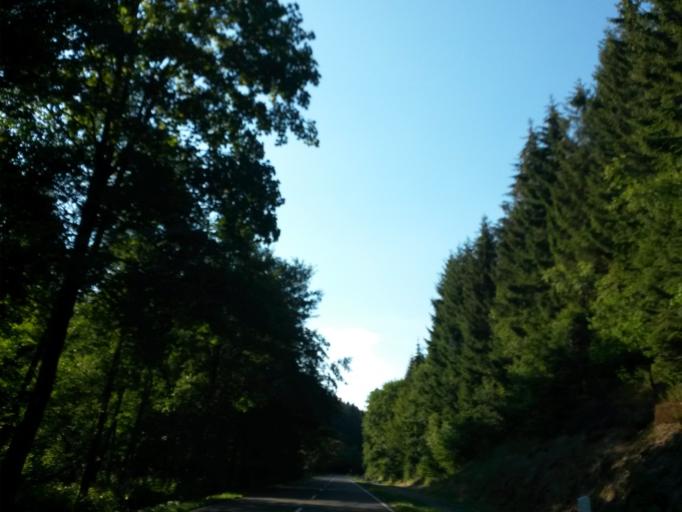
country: DE
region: North Rhine-Westphalia
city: Meinerzhagen
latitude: 51.0693
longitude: 7.6518
